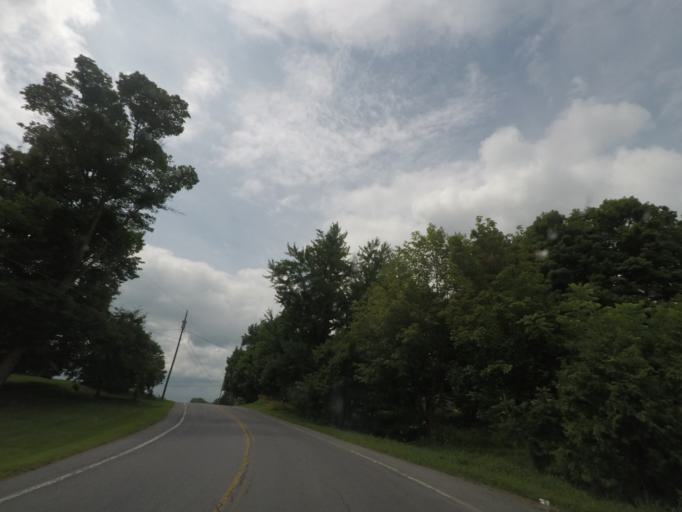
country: US
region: New York
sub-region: Saratoga County
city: Saratoga Springs
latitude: 43.0680
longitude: -73.6830
